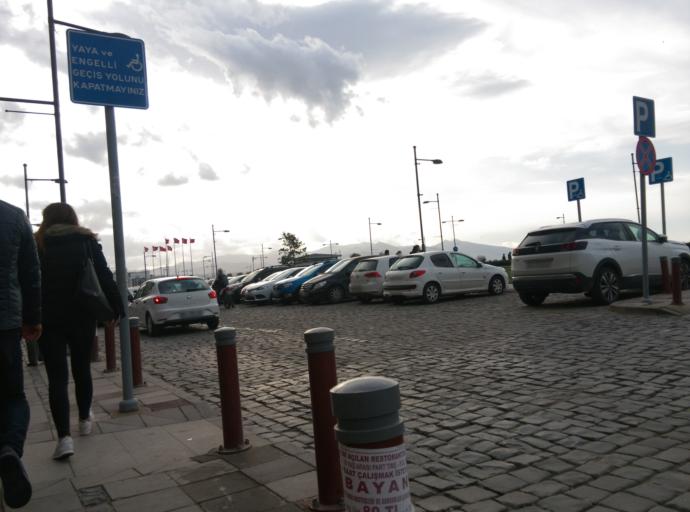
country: TR
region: Izmir
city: Izmir
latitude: 38.4401
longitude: 27.1422
